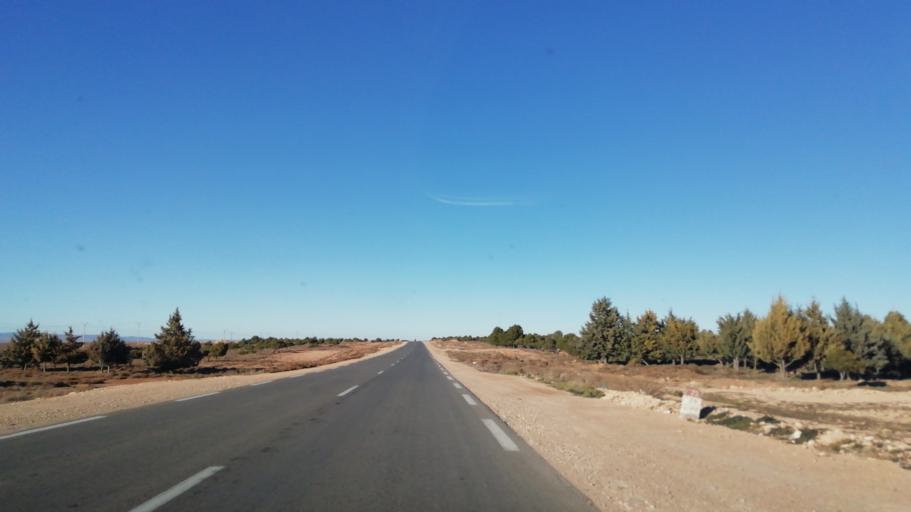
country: DZ
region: Tlemcen
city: Sebdou
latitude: 34.2689
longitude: -1.2583
